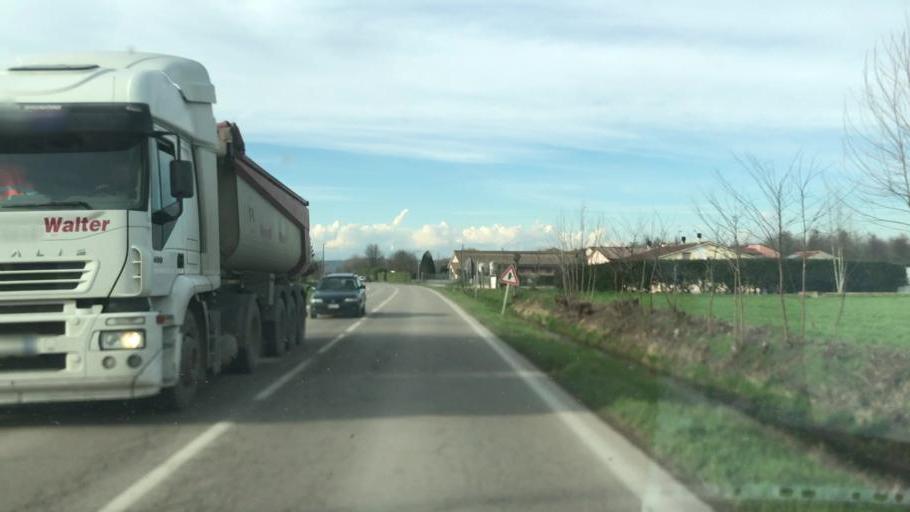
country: IT
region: Lombardy
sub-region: Provincia di Mantova
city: Cerlongo
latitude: 45.2855
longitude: 10.6574
